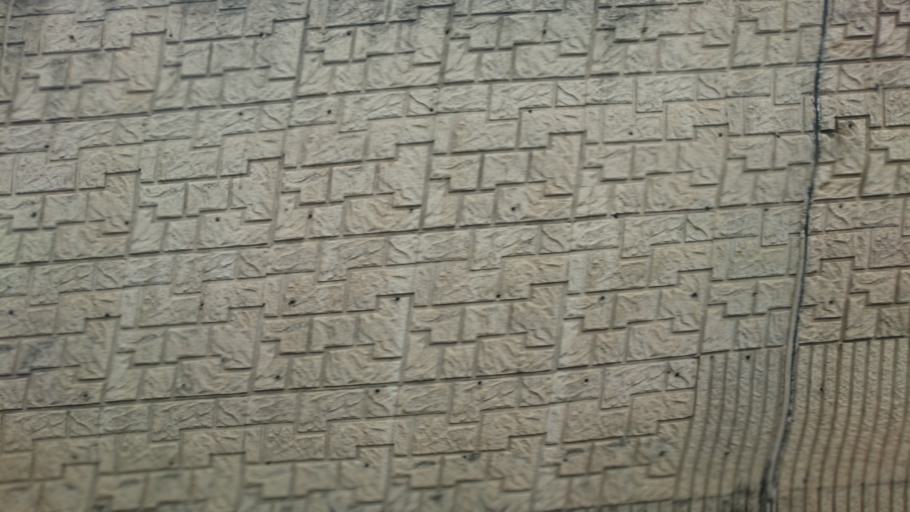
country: KR
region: Daegu
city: Daegu
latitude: 35.8785
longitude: 128.6511
